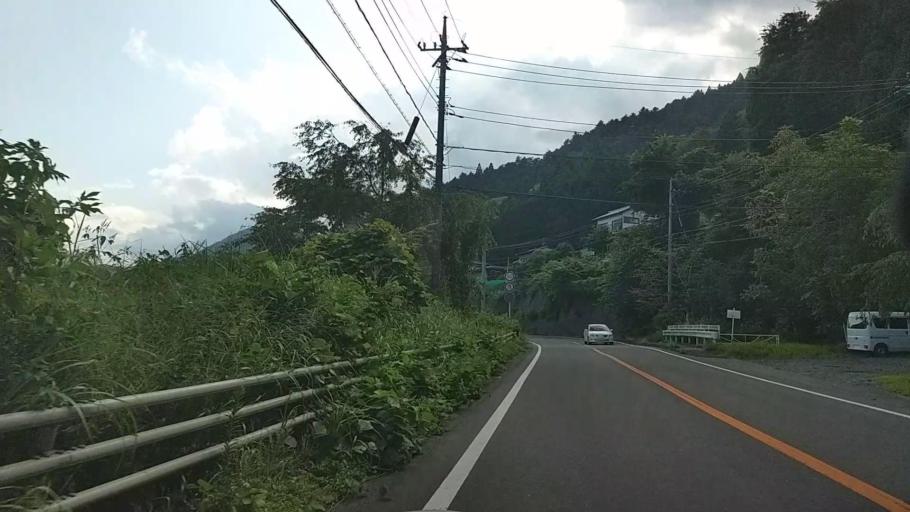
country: JP
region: Shizuoka
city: Fujinomiya
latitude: 35.3648
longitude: 138.4221
